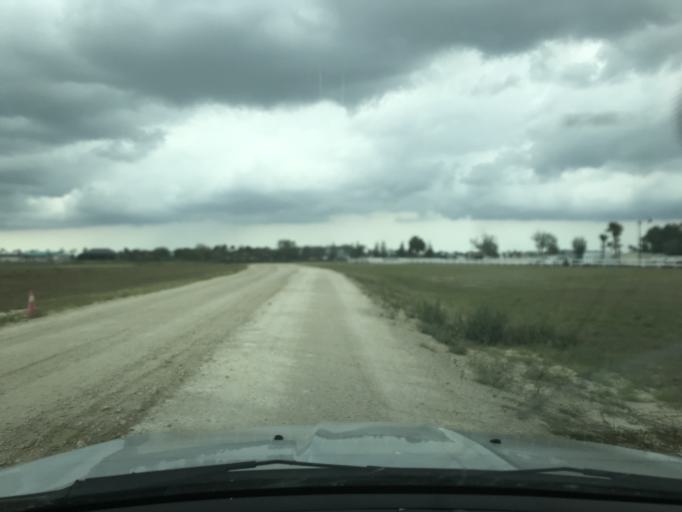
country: US
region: Florida
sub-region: Lee County
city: Olga
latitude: 26.7822
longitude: -81.7465
